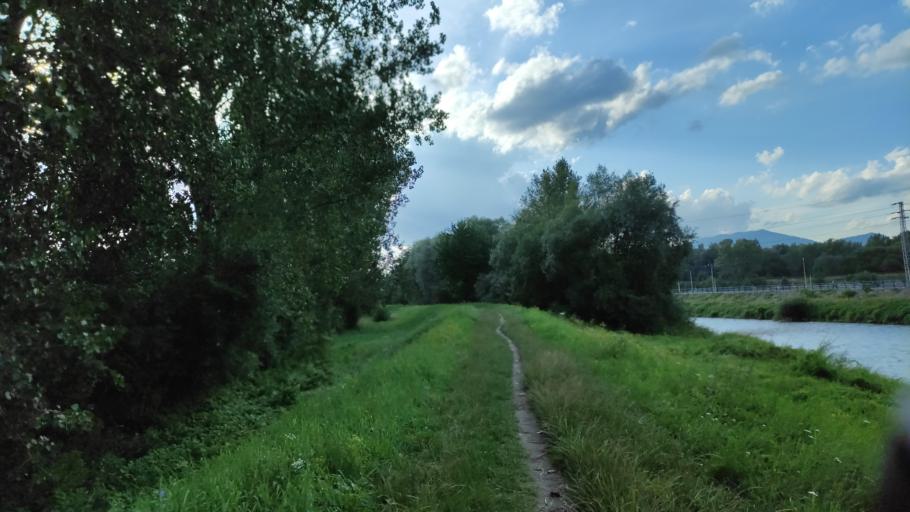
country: SK
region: Zilinsky
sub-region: Okres Liptovsky Mikulas
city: Liptovsky Mikulas
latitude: 49.0897
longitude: 19.5900
